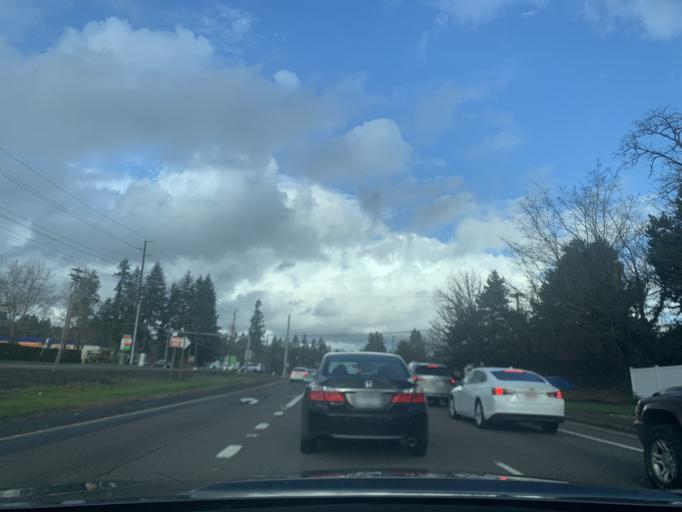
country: US
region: Oregon
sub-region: Washington County
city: King City
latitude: 45.3969
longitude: -122.7986
